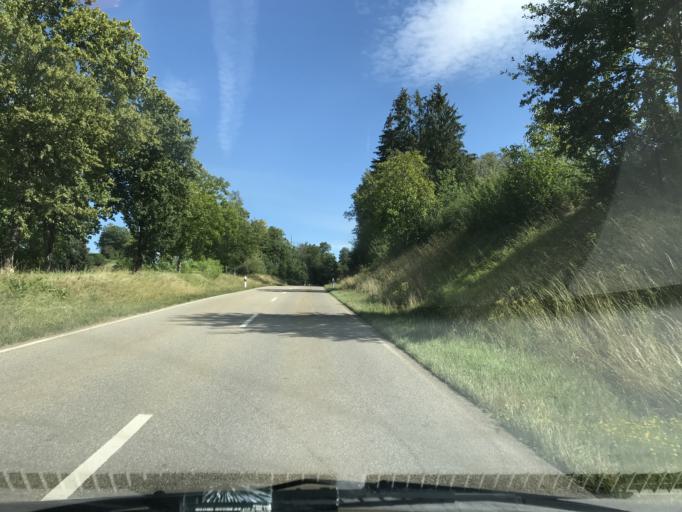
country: DE
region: Baden-Wuerttemberg
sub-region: Freiburg Region
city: Schopfheim
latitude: 47.6421
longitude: 7.8347
